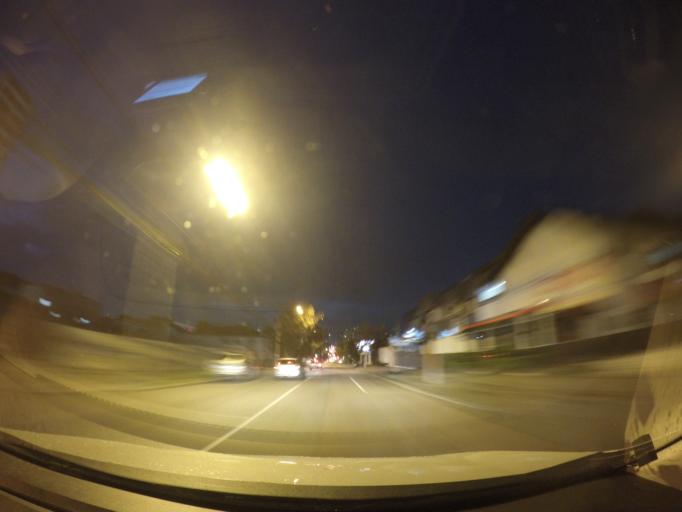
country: BR
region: Parana
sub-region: Curitiba
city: Curitiba
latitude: -25.4511
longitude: -49.2719
